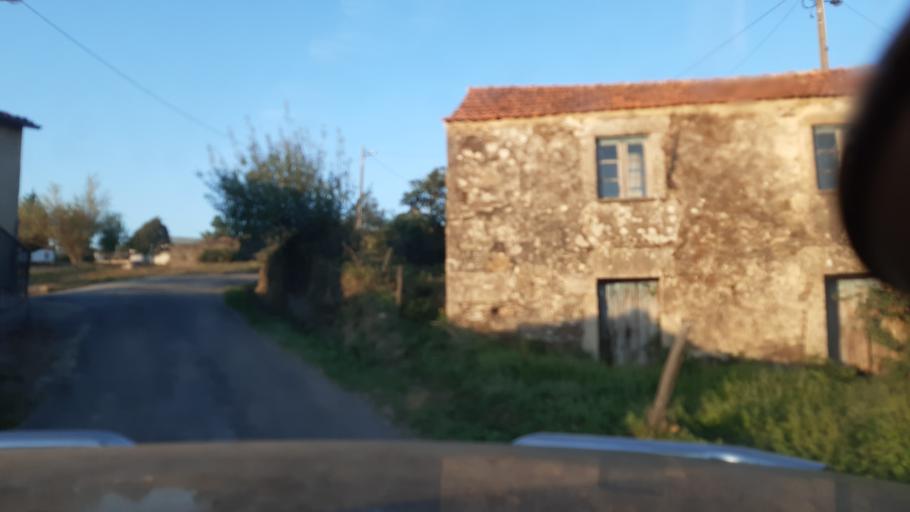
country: PT
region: Viseu
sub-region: Mortagua
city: Mortagua
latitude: 40.5441
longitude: -8.2618
